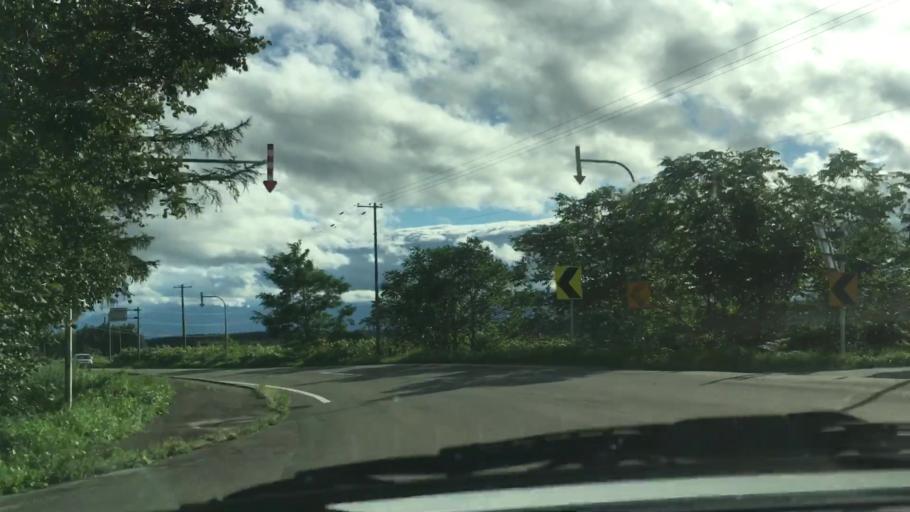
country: JP
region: Hokkaido
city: Otofuke
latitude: 43.1791
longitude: 143.0082
